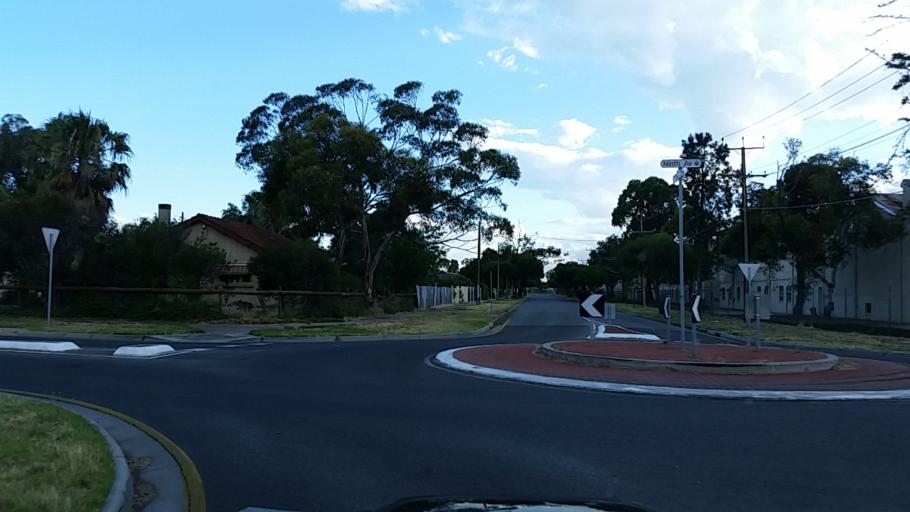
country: AU
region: South Australia
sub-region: Charles Sturt
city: Woodville North
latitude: -34.8625
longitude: 138.5430
